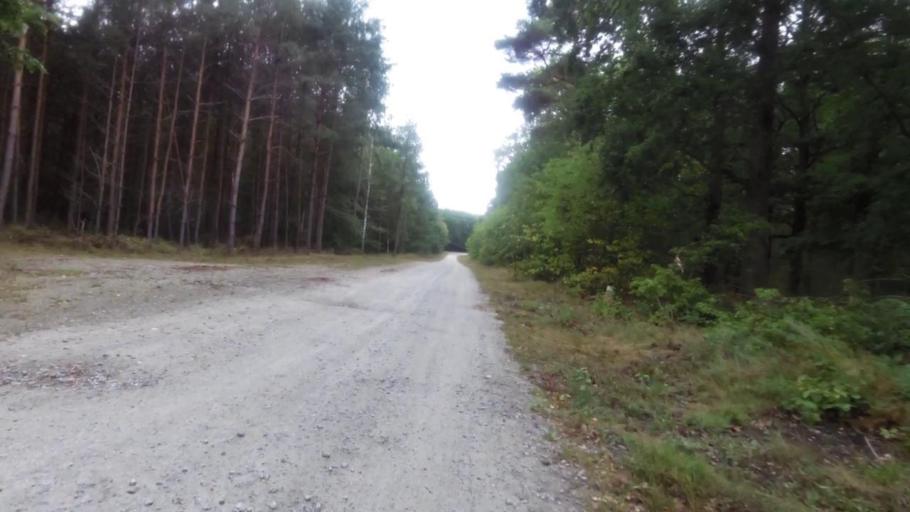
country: PL
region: Lubusz
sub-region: Powiat gorzowski
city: Kostrzyn nad Odra
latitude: 52.6218
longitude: 14.6514
